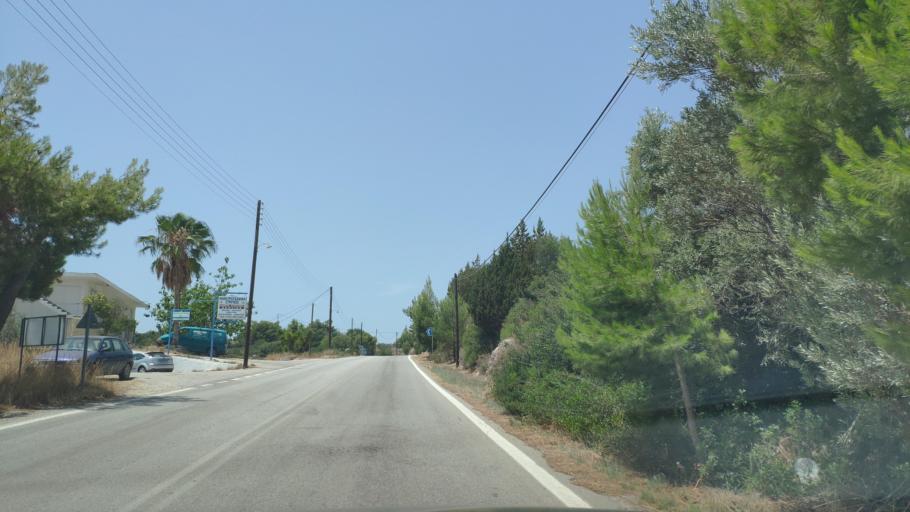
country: GR
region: Peloponnese
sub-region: Nomos Argolidos
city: Kranidi
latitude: 37.3741
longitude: 23.1513
